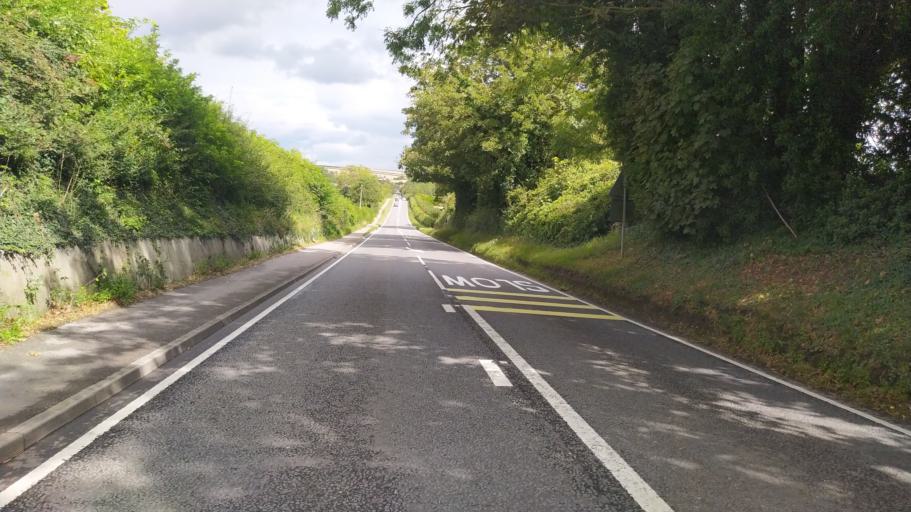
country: GB
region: England
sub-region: Dorset
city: Blandford Forum
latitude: 50.8726
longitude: -2.1443
